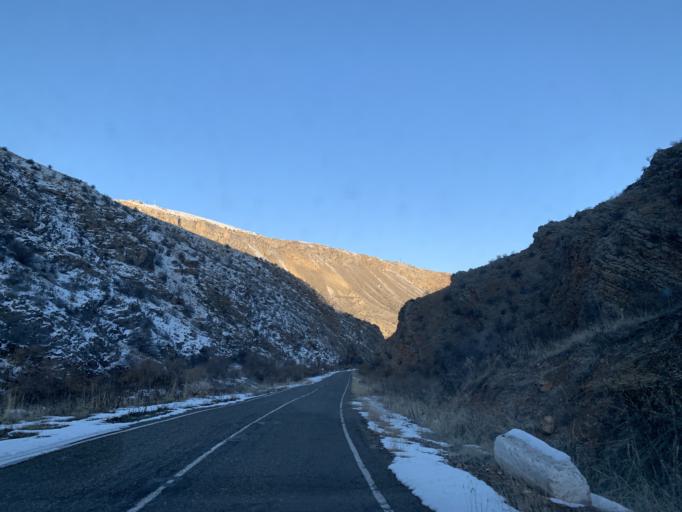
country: AM
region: Vayots' Dzori Marz
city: Areni
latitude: 39.6911
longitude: 45.2182
